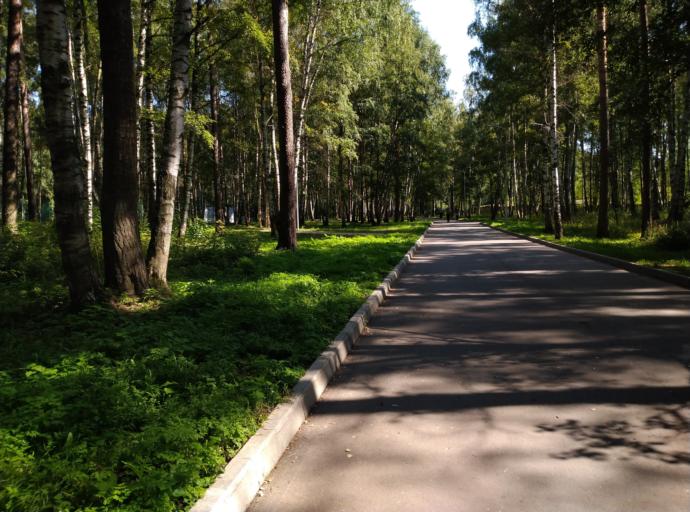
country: RU
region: Kostroma
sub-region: Kostromskoy Rayon
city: Kostroma
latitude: 57.7939
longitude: 40.9636
